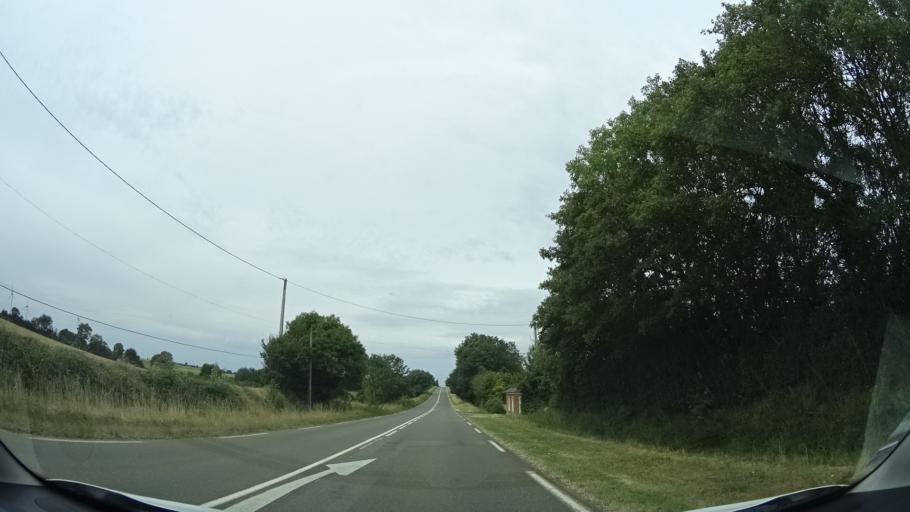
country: FR
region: Pays de la Loire
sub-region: Departement de la Mayenne
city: Meslay-du-Maine
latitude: 47.9163
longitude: -0.4686
